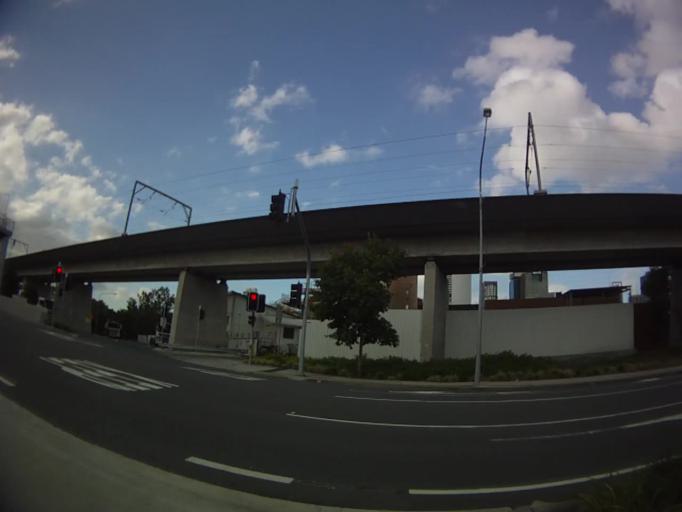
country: AU
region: Queensland
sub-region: Brisbane
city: Milton
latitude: -27.4715
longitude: 153.0138
